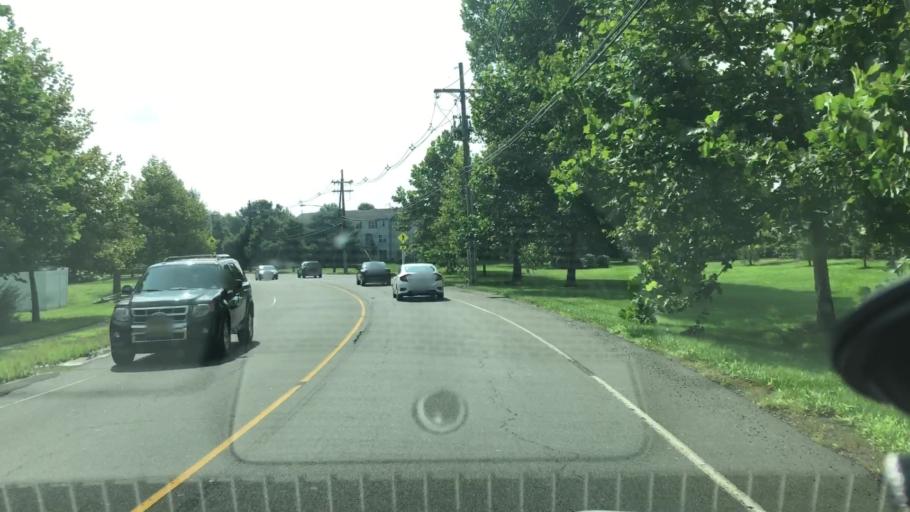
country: US
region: New Jersey
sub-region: Mercer County
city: Lawrenceville
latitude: 40.3017
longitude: -74.6876
